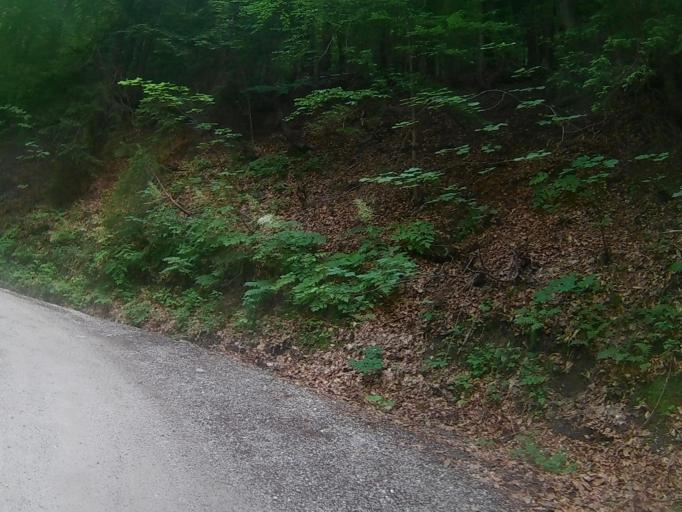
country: SI
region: Ruse
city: Ruse
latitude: 46.5243
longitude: 15.5378
